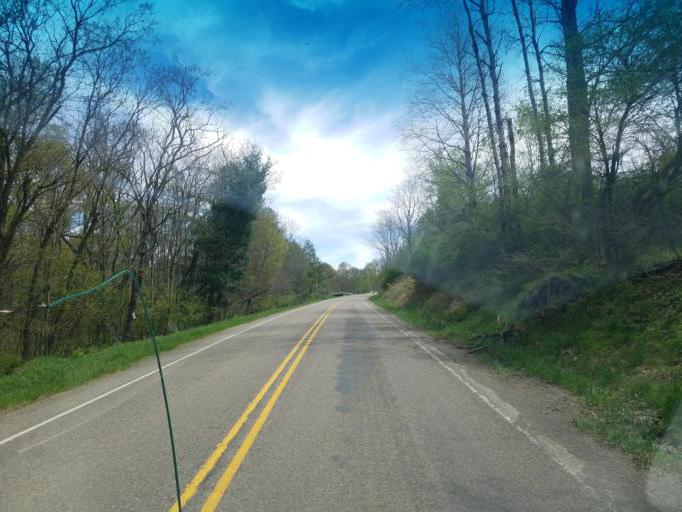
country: US
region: Pennsylvania
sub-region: Tioga County
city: Wellsboro
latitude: 41.7296
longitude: -77.4116
